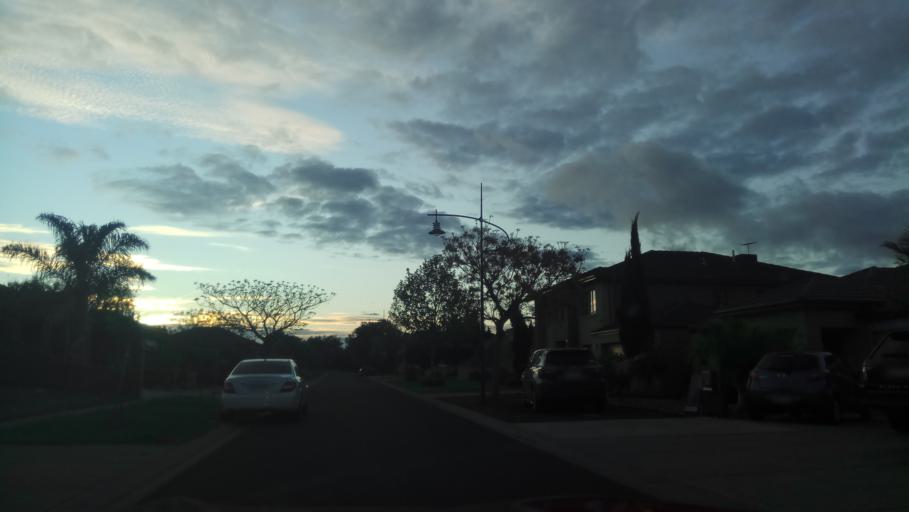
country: AU
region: Victoria
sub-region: Wyndham
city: Point Cook
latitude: -37.8976
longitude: 144.7389
